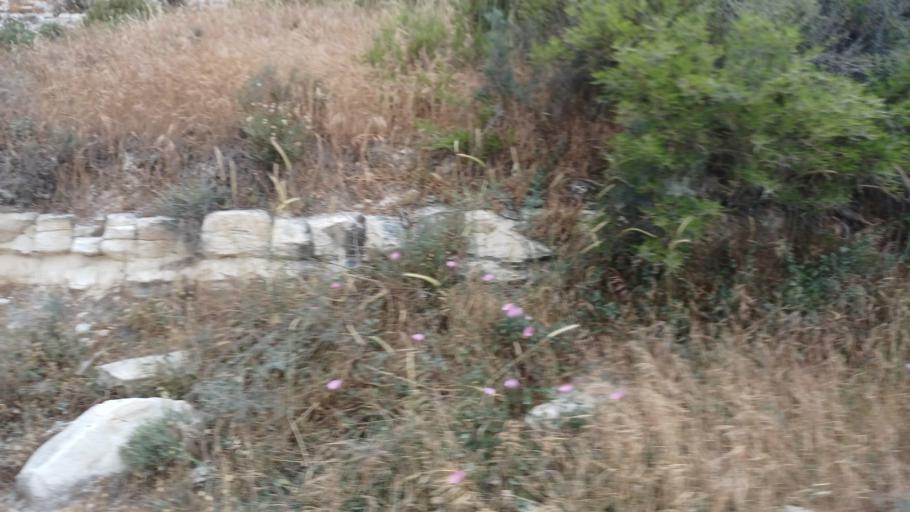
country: CY
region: Larnaka
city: Athienou
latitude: 35.0254
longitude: 33.5558
